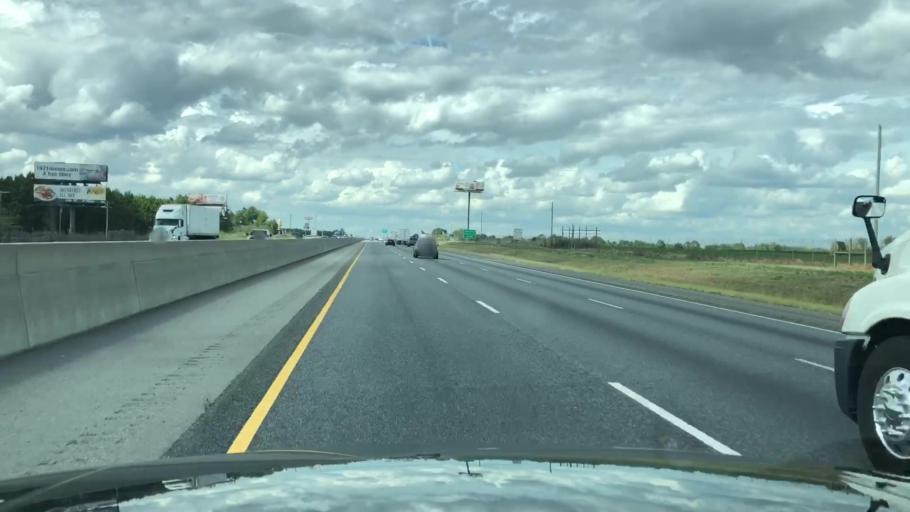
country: US
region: Georgia
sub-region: Turner County
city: Ashburn
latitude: 31.7016
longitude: -83.6325
